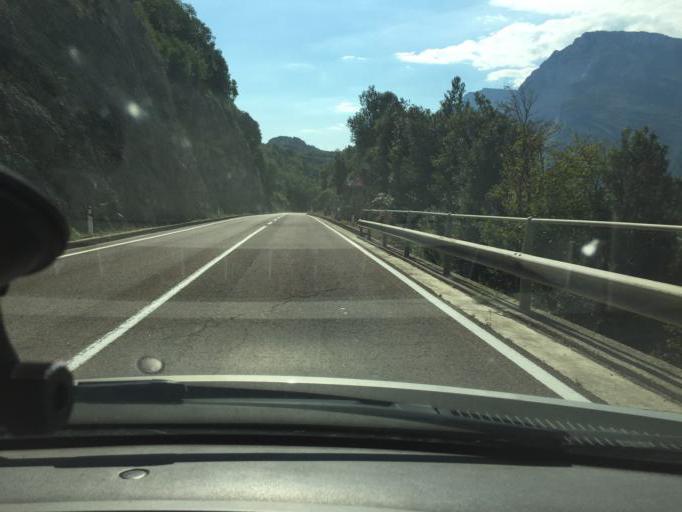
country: IT
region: Trentino-Alto Adige
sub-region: Provincia di Trento
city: Padergnone
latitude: 46.0647
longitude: 10.9892
